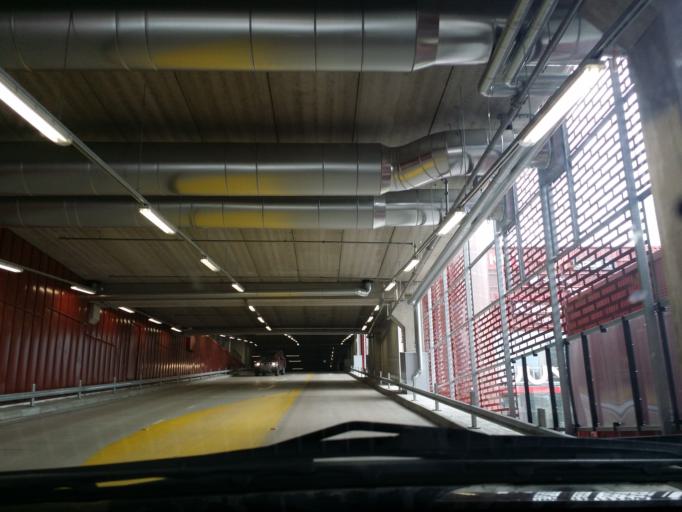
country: FI
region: Satakunta
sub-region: Pori
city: Pori
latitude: 61.4952
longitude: 21.7986
